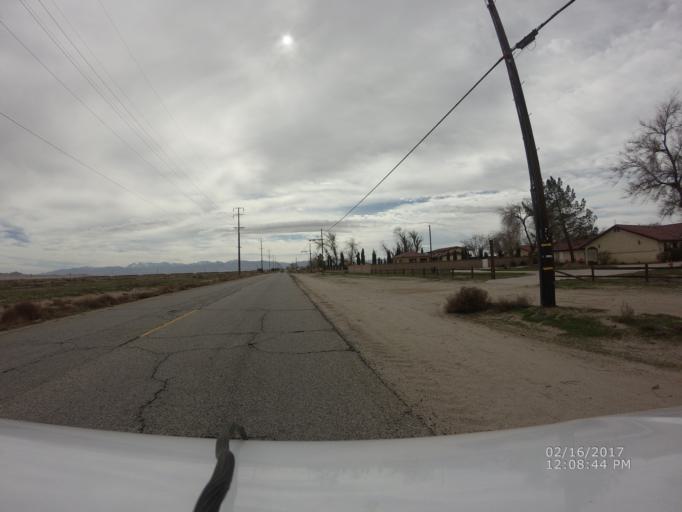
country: US
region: California
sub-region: Los Angeles County
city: Lake Los Angeles
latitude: 34.6864
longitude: -117.9698
